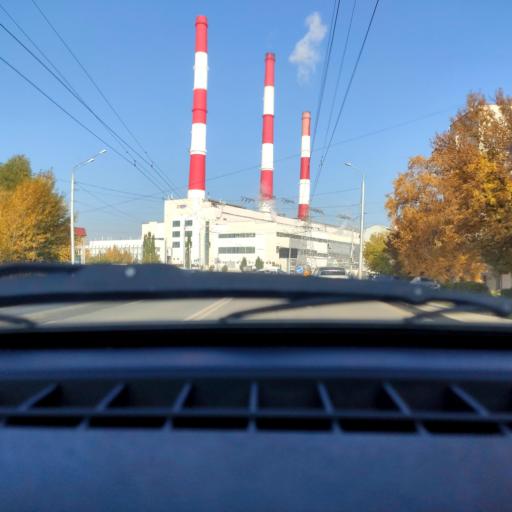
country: RU
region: Bashkortostan
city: Ufa
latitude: 54.7867
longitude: 56.1227
